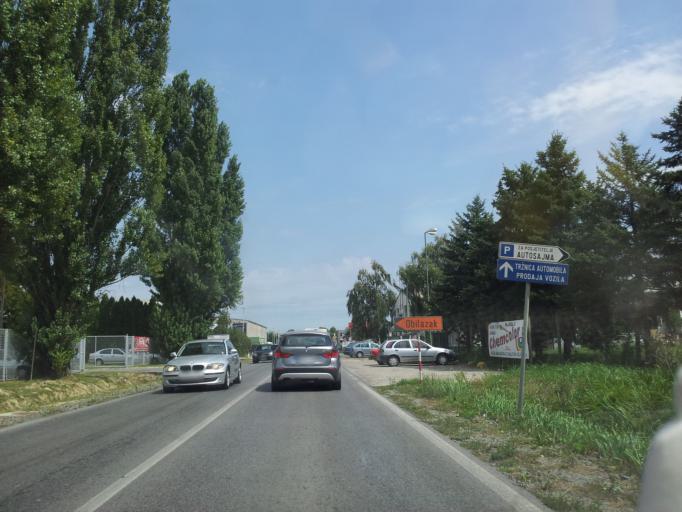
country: HR
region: Osjecko-Baranjska
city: Brijest
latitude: 45.5394
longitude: 18.6478
